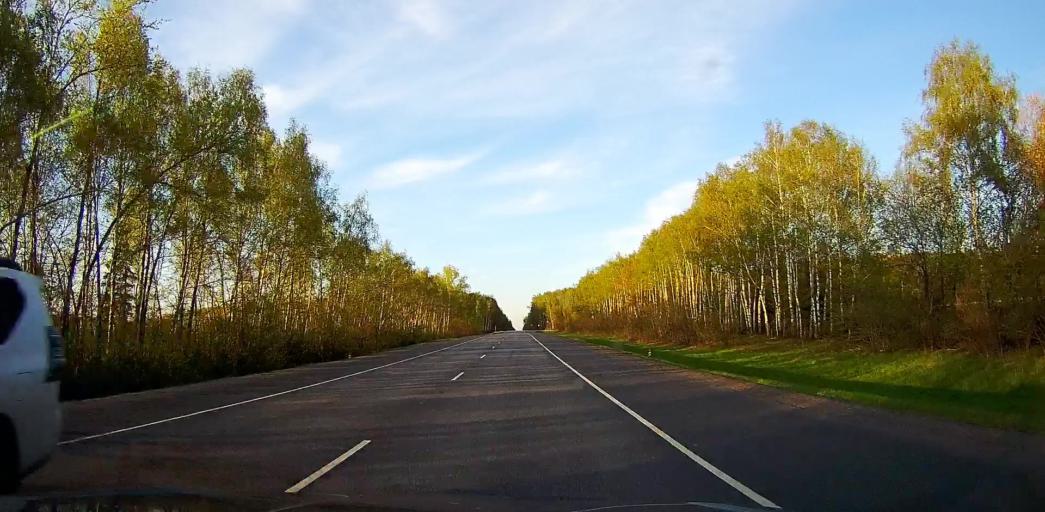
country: RU
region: Moskovskaya
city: Meshcherino
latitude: 55.2461
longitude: 38.4383
